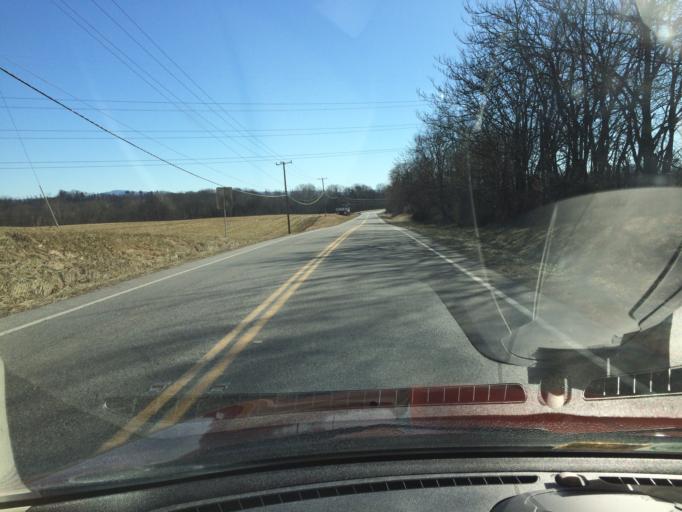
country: US
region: Virginia
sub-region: Rockingham County
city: Bridgewater
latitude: 38.3499
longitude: -78.9440
